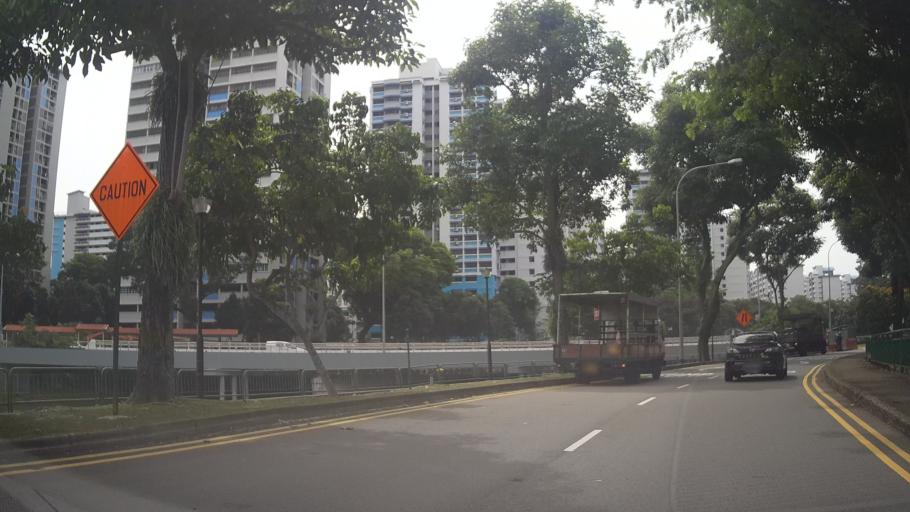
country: SG
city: Singapore
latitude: 1.3246
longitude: 103.8668
